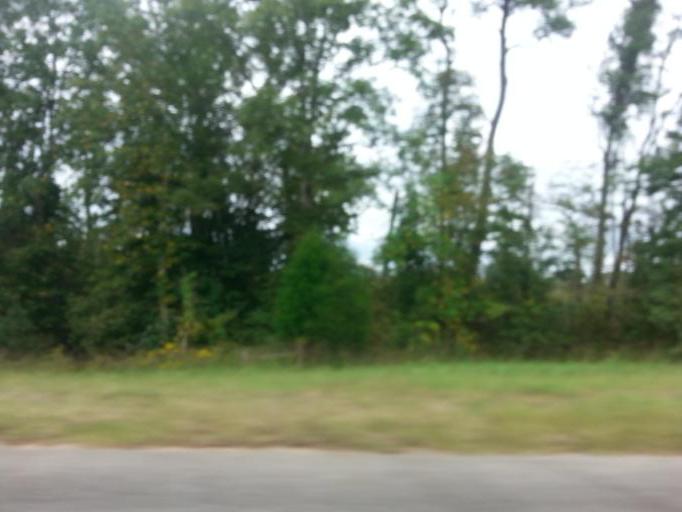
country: US
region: Alabama
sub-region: Butler County
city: Georgiana
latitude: 31.6395
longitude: -86.7866
